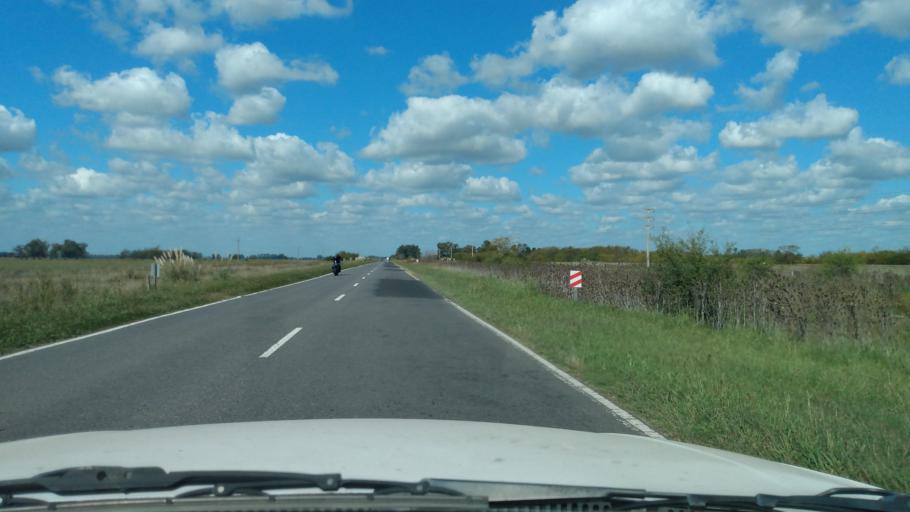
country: AR
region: Buenos Aires
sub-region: Partido de Navarro
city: Navarro
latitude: -34.8942
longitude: -59.3365
